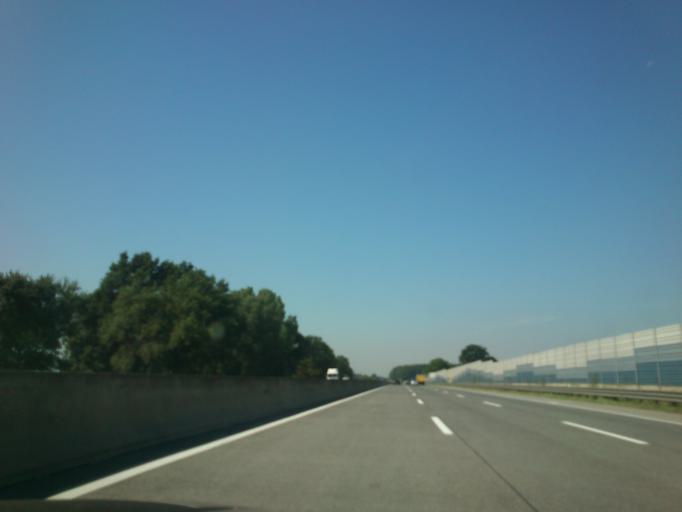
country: AT
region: Upper Austria
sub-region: Politischer Bezirk Linz-Land
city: Horsching
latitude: 48.1818
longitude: 14.1904
